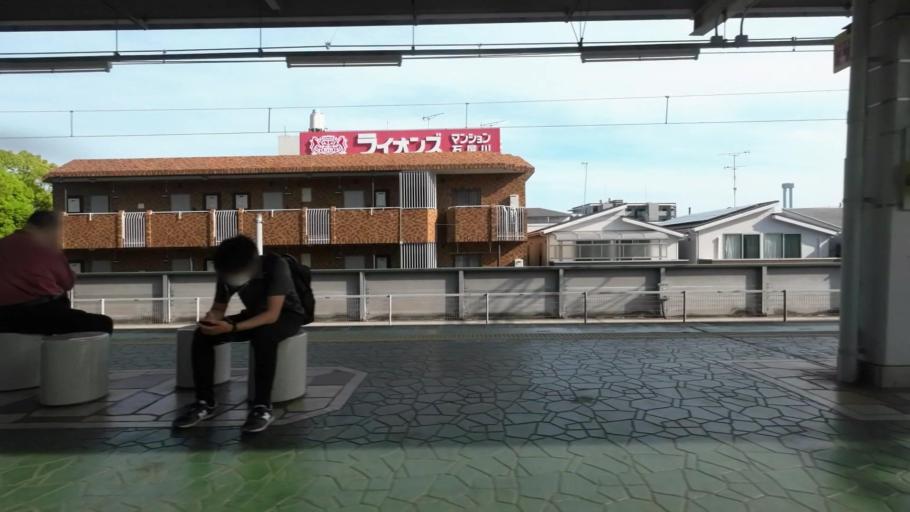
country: JP
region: Hyogo
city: Ashiya
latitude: 34.7133
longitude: 135.2493
